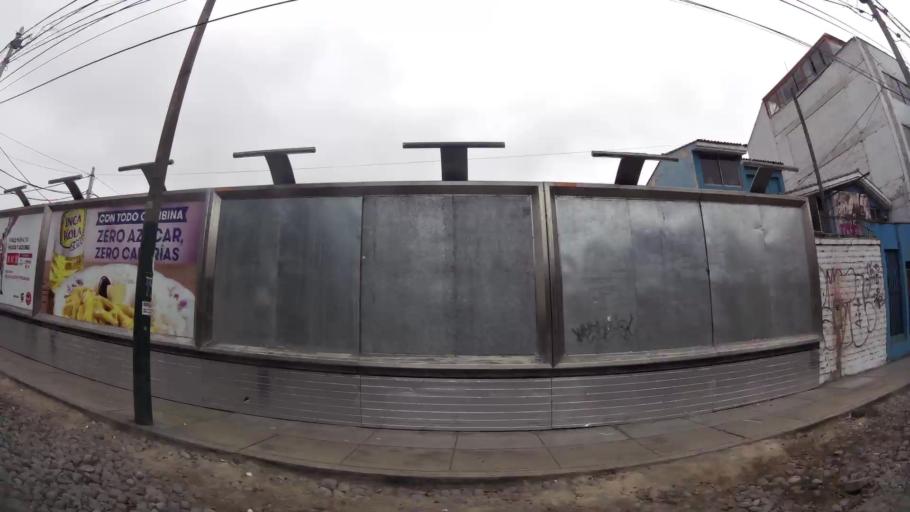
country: PE
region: Lima
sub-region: Lima
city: Surco
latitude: -12.1203
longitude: -76.9967
